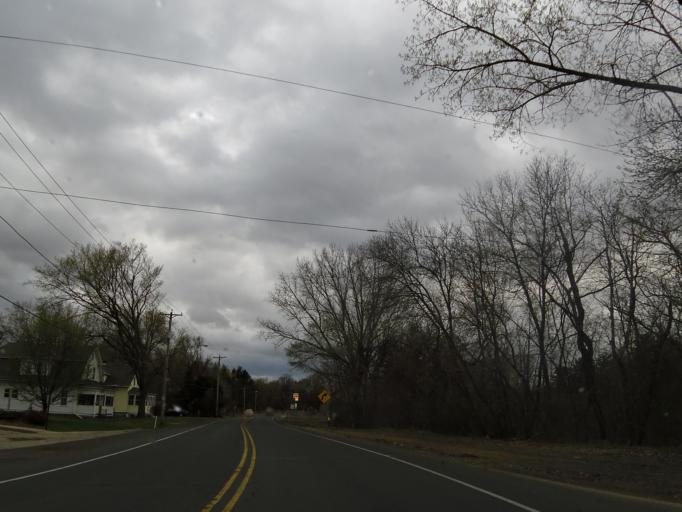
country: US
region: Wisconsin
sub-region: Saint Croix County
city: North Hudson
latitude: 45.0216
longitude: -92.6676
